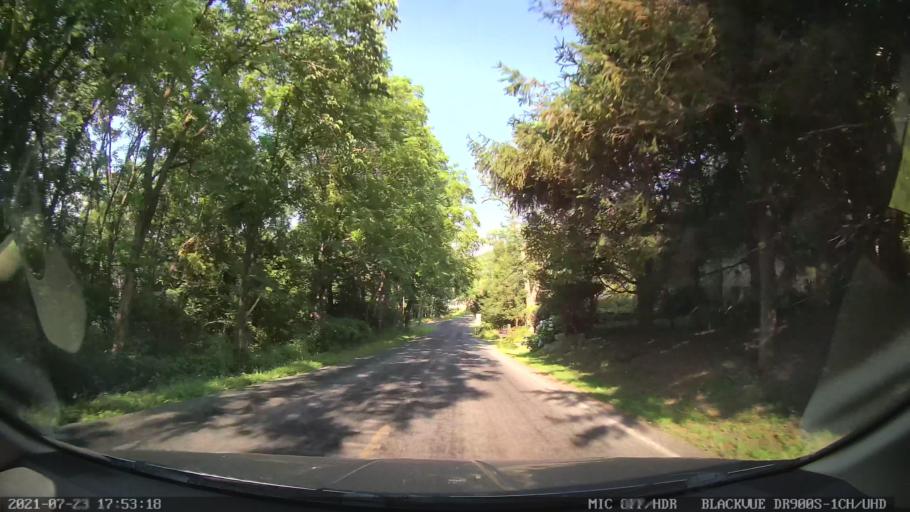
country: US
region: Pennsylvania
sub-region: Lehigh County
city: Macungie
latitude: 40.5046
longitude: -75.5670
